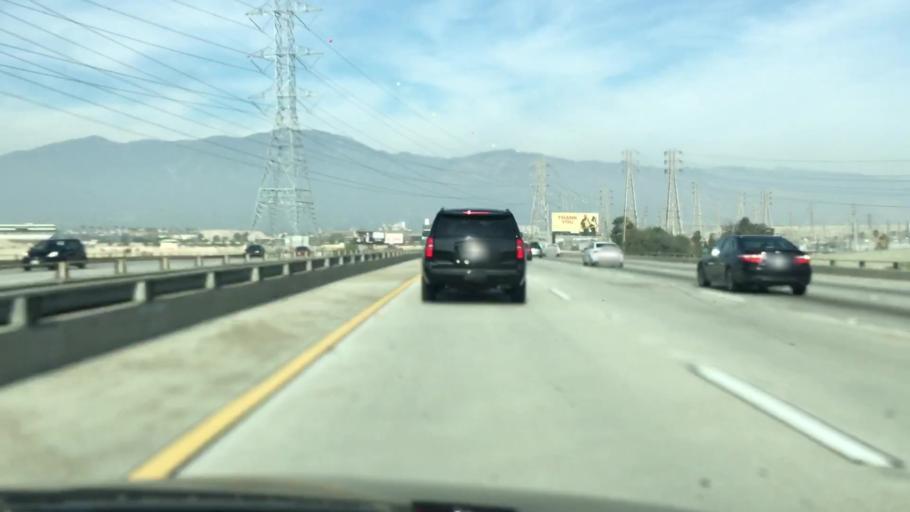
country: US
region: California
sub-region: Los Angeles County
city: Baldwin Park
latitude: 34.0997
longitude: -117.9849
